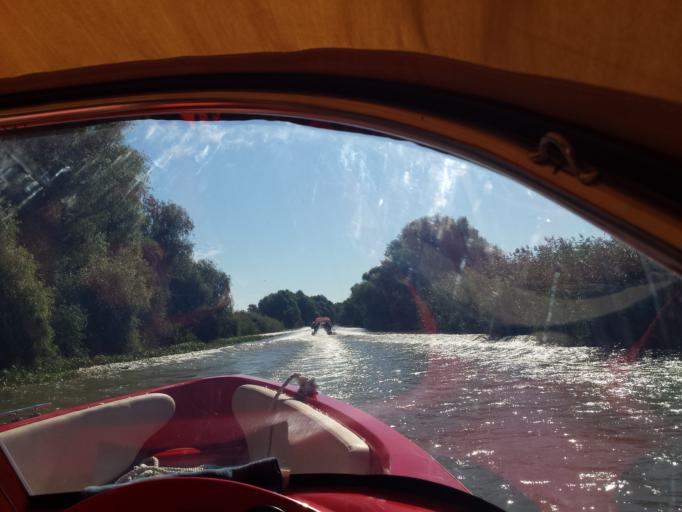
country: RO
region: Tulcea
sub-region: Comuna Pardina
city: Pardina
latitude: 45.2484
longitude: 29.0524
